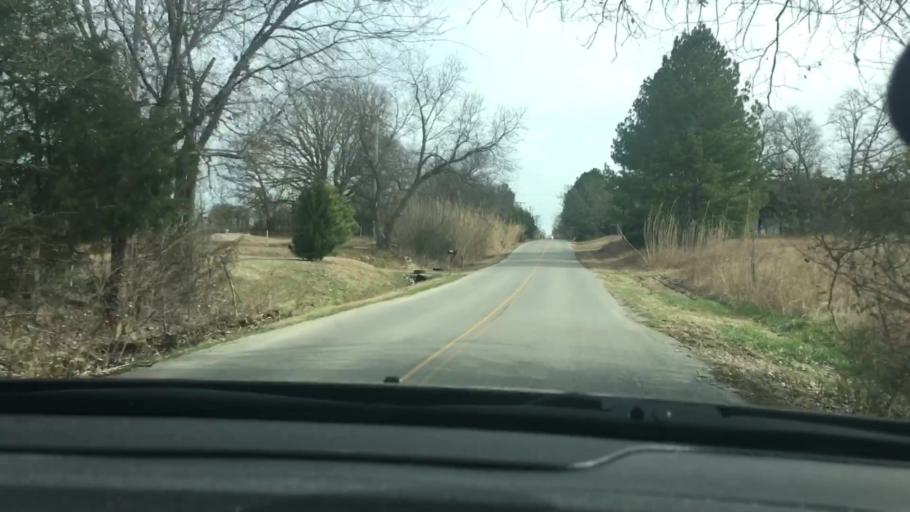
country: US
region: Oklahoma
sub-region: Carter County
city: Ardmore
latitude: 34.1728
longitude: -97.0763
